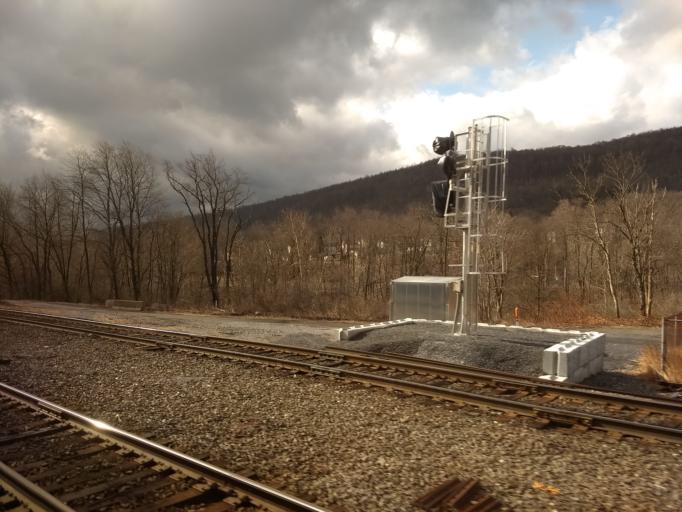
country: US
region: Pennsylvania
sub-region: Cambria County
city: Vinco
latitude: 40.3665
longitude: -78.7982
